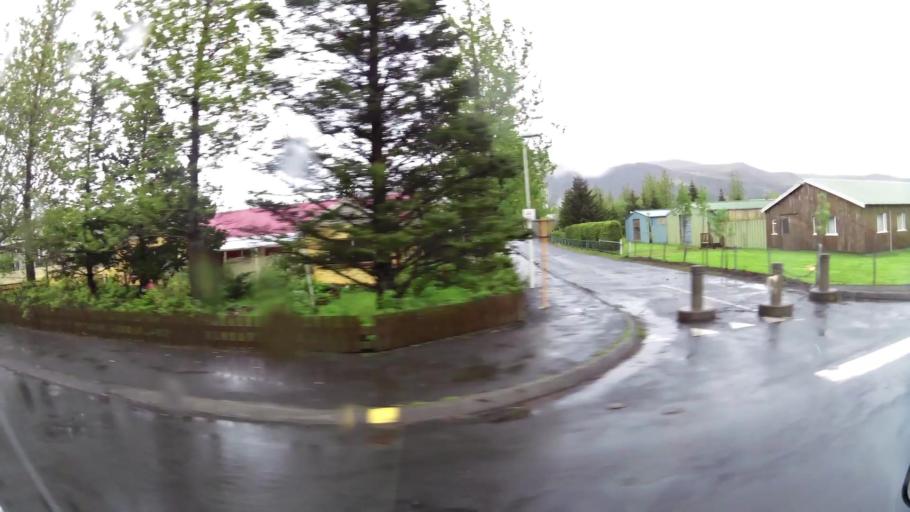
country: IS
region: South
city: Hveragerdi
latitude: 63.9999
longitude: -21.1938
